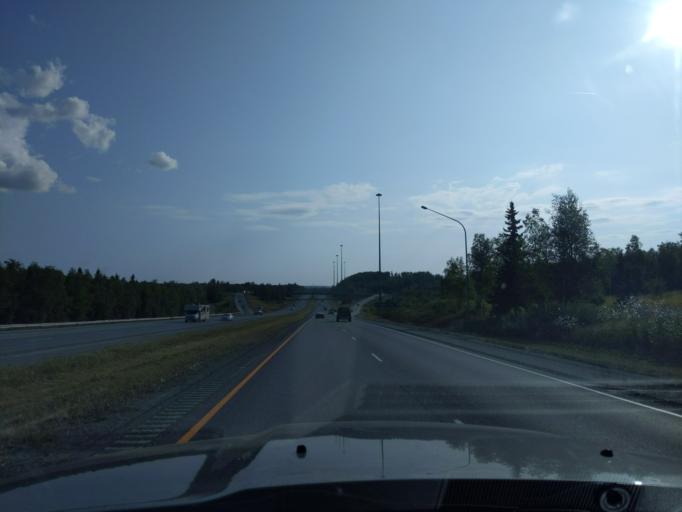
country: US
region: Alaska
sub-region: Anchorage Municipality
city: Eagle River
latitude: 61.3467
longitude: -149.5566
